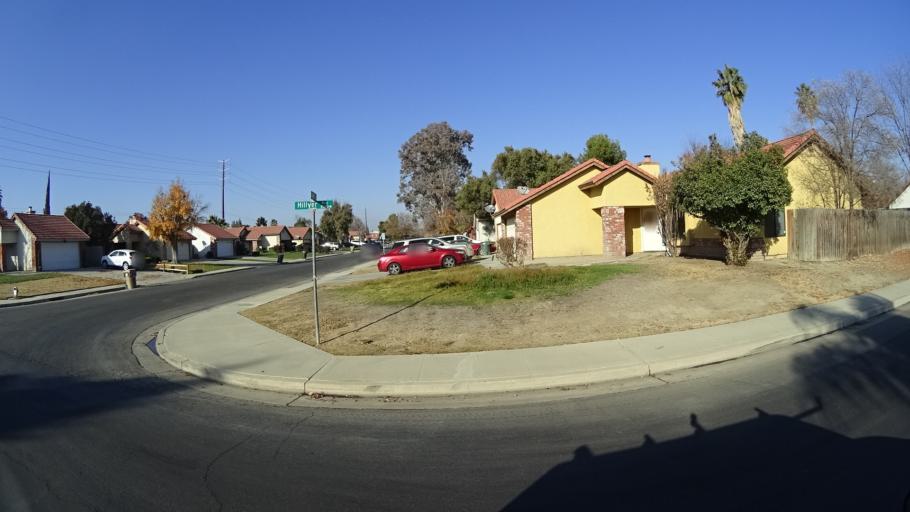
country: US
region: California
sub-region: Kern County
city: Greenacres
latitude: 35.3115
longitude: -119.0957
